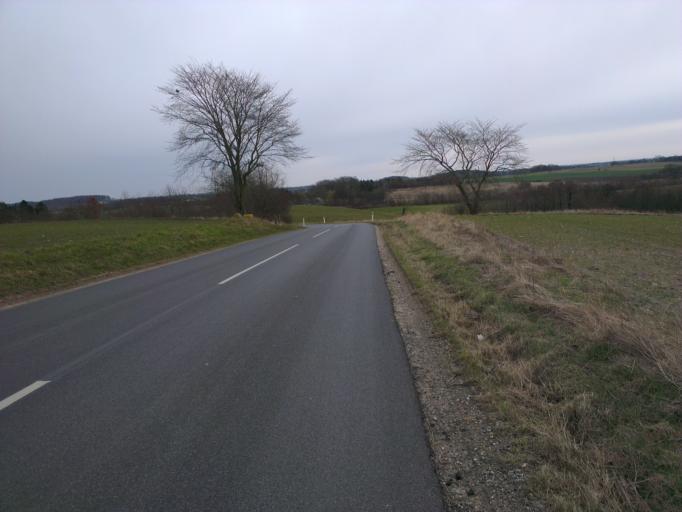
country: DK
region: Capital Region
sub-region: Frederikssund Kommune
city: Skibby
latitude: 55.7667
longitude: 11.9021
